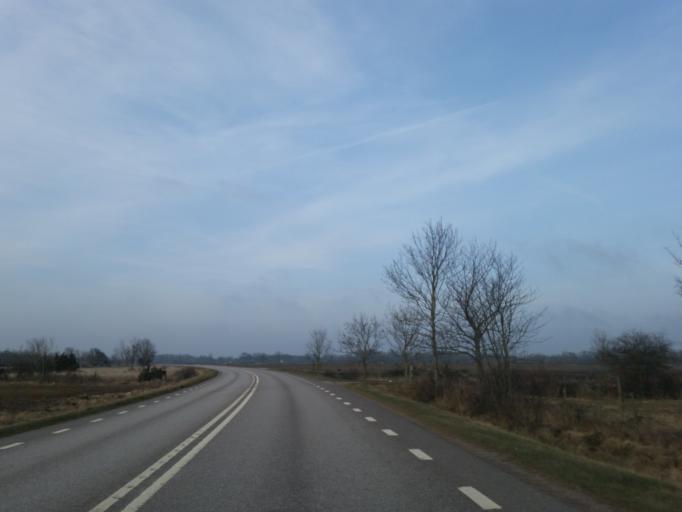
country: SE
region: Kalmar
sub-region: Borgholms Kommun
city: Borgholm
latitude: 56.8861
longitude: 16.7301
